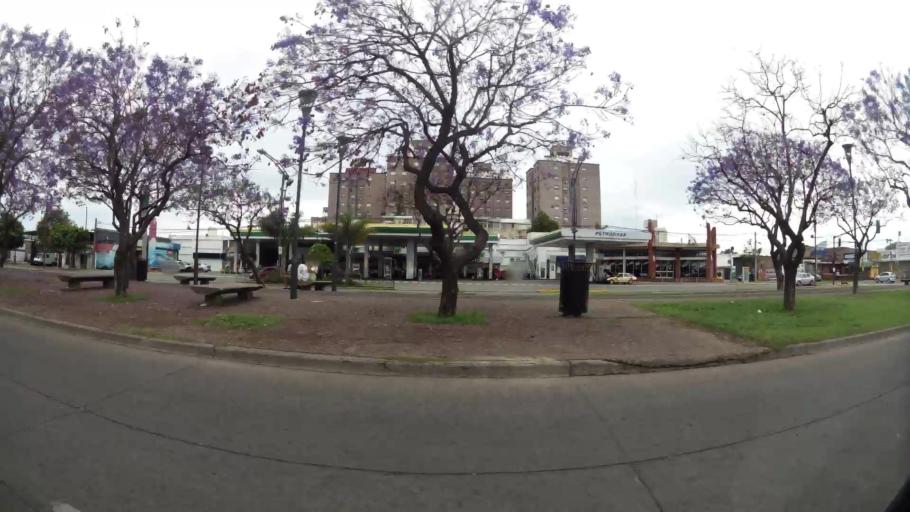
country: AR
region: Santa Fe
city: Gobernador Galvez
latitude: -32.9972
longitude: -60.6654
